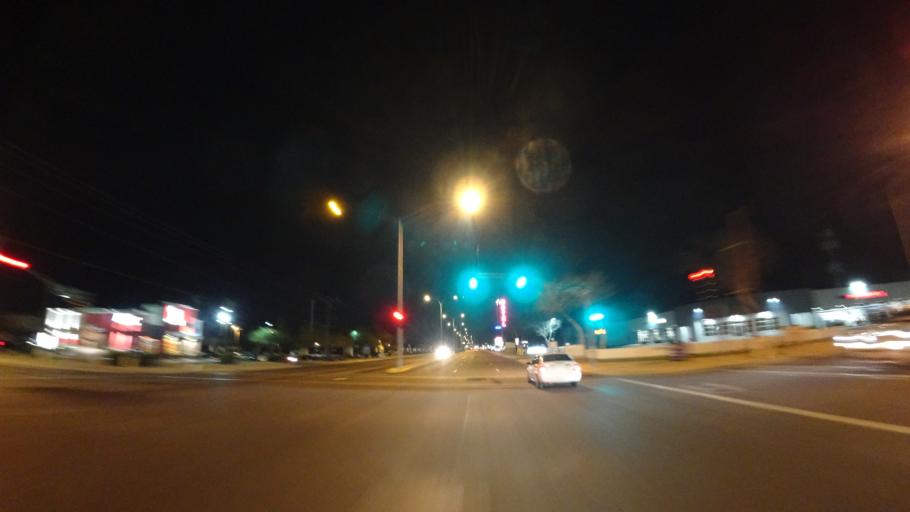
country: US
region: Arizona
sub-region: Maricopa County
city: Mesa
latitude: 33.4155
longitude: -111.7710
